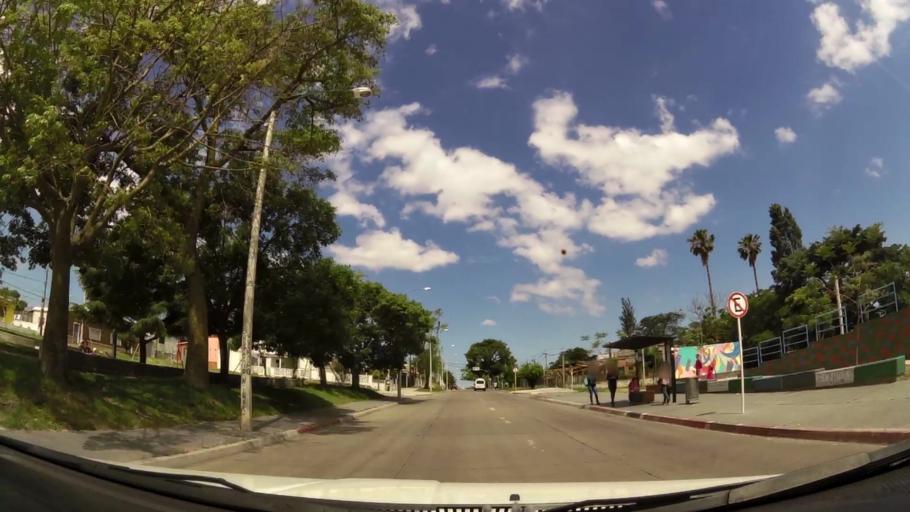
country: UY
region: Montevideo
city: Montevideo
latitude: -34.8437
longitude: -56.2418
